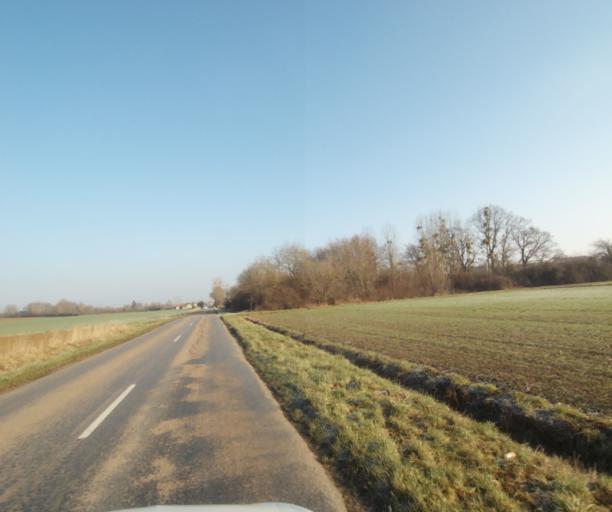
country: FR
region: Champagne-Ardenne
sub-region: Departement de la Haute-Marne
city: Montier-en-Der
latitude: 48.4492
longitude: 4.7643
